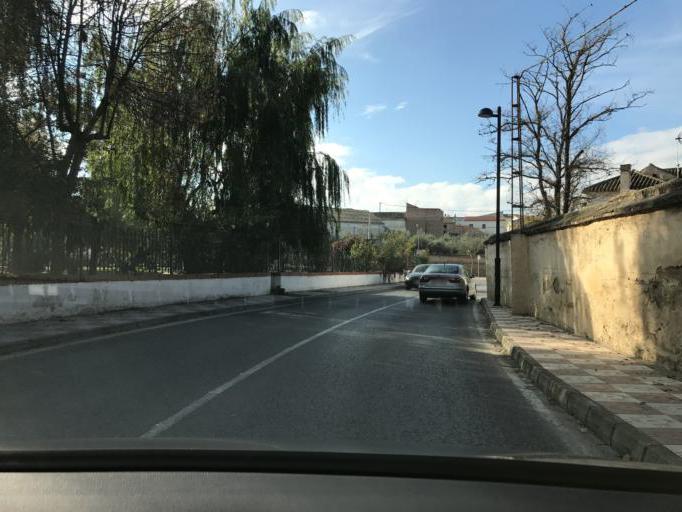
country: ES
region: Andalusia
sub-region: Provincia de Granada
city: Otura
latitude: 37.0959
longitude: -3.6361
